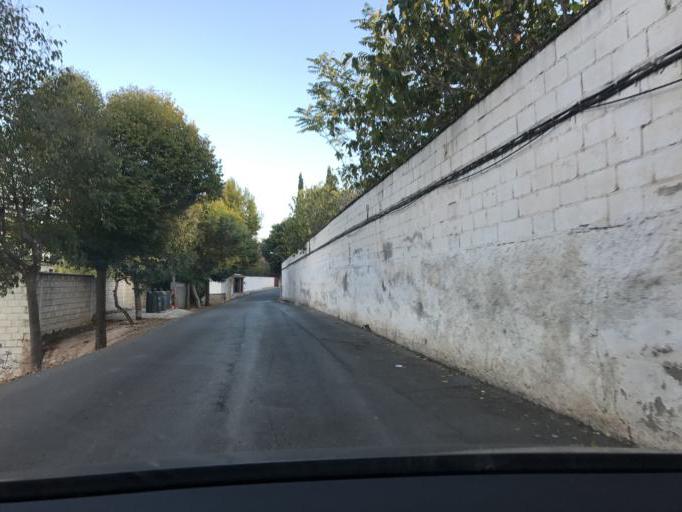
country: ES
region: Andalusia
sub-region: Provincia de Granada
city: Jun
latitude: 37.2212
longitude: -3.5962
